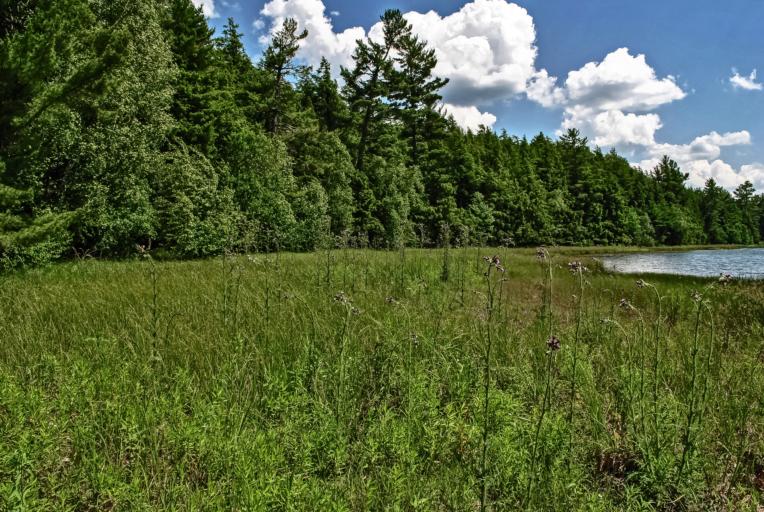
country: US
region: Michigan
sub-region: Iron County
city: Stambaugh, Iron River
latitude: 45.8815
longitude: -88.5561
